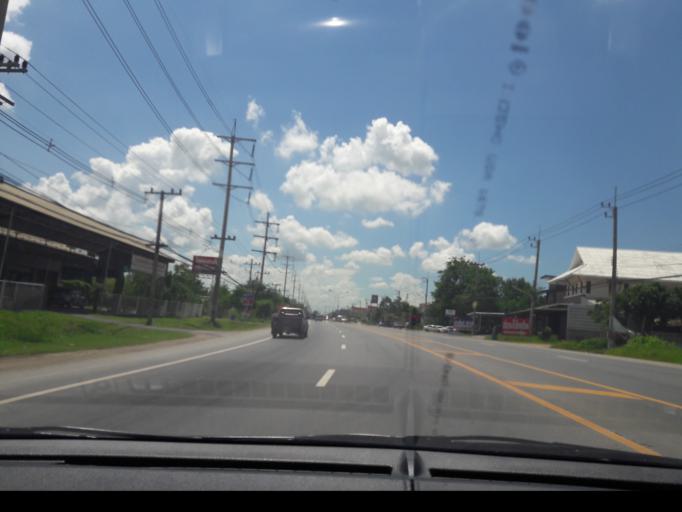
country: TH
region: Nakhon Pathom
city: Kamphaeng Saen
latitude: 14.0089
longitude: 100.0005
